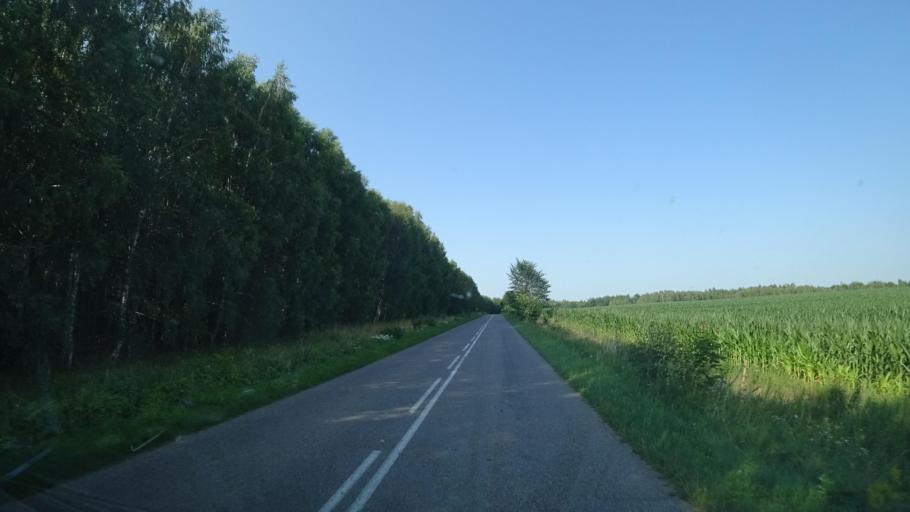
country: PL
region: Pomeranian Voivodeship
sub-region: Powiat czluchowski
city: Rzeczenica
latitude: 53.7832
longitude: 17.1662
